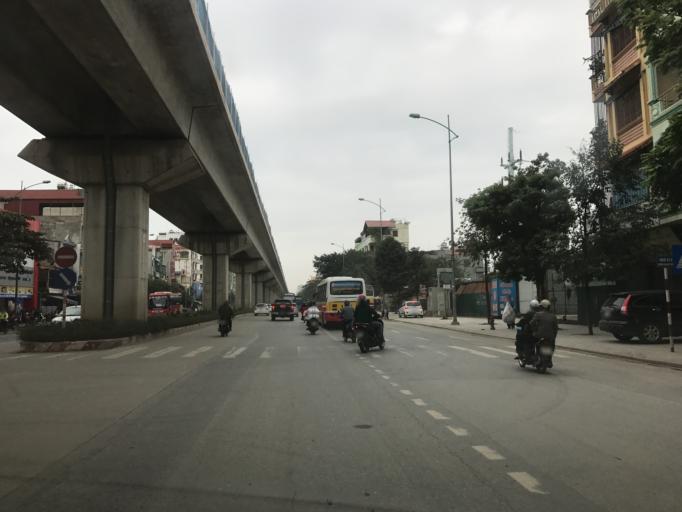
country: VN
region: Ha Noi
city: Ha Dong
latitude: 20.9575
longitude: 105.7586
